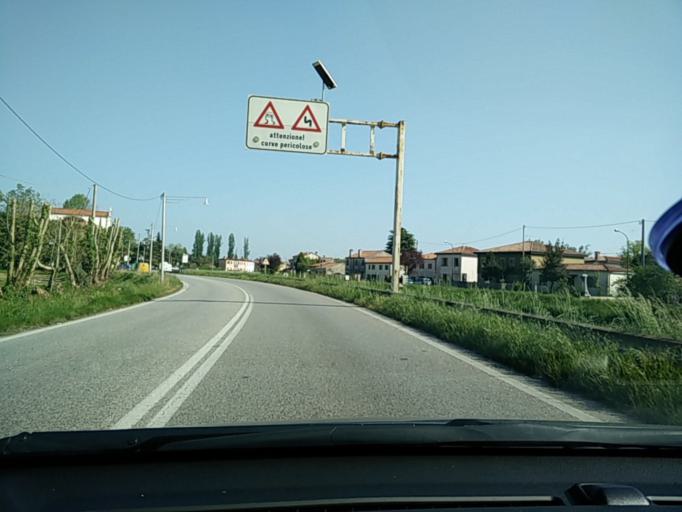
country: IT
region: Veneto
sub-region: Provincia di Venezia
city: Fornase
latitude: 45.4521
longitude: 12.1814
